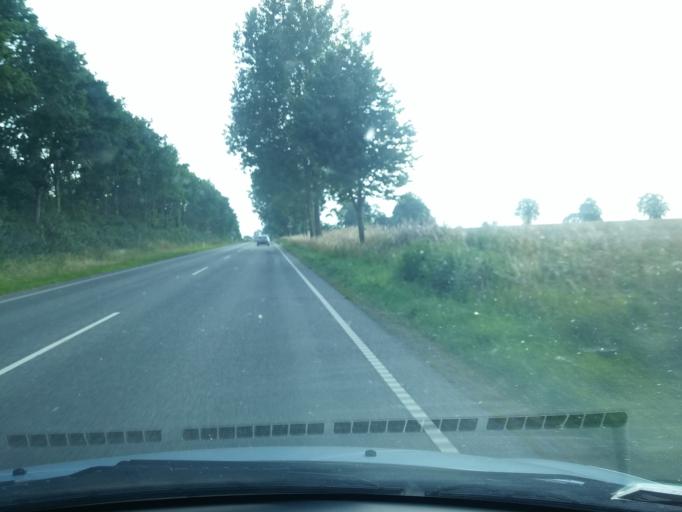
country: DK
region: South Denmark
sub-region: Odense Kommune
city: Bellinge
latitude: 55.3437
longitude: 10.3200
